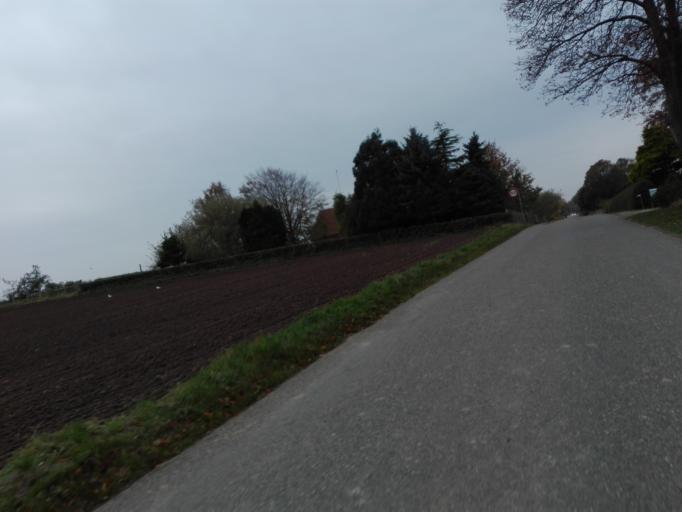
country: DK
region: Central Jutland
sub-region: Arhus Kommune
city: Beder
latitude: 56.0480
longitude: 10.2398
